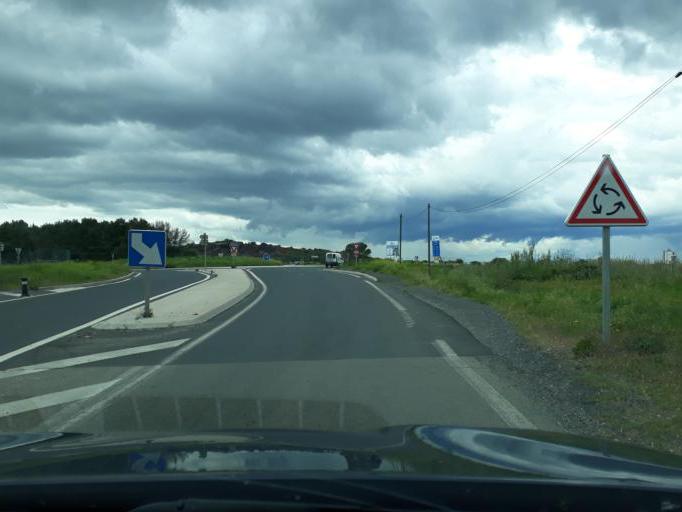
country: FR
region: Languedoc-Roussillon
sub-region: Departement de l'Herault
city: Bessan
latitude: 43.3723
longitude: 3.4219
